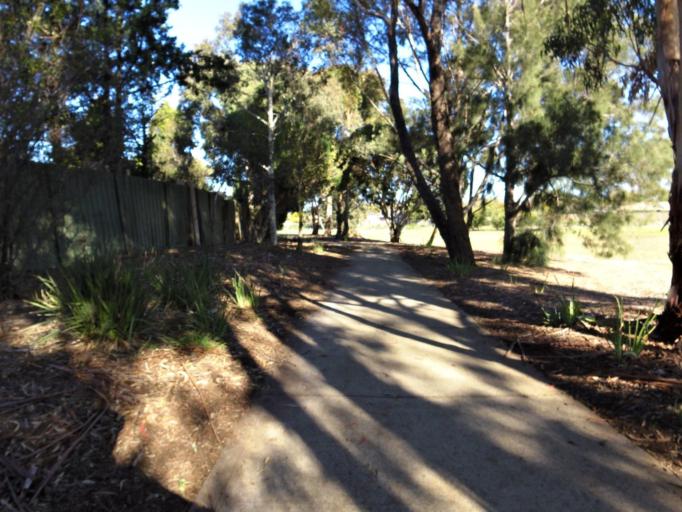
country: AU
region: Victoria
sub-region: Wyndham
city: Tarneit
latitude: -37.8737
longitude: 144.6736
